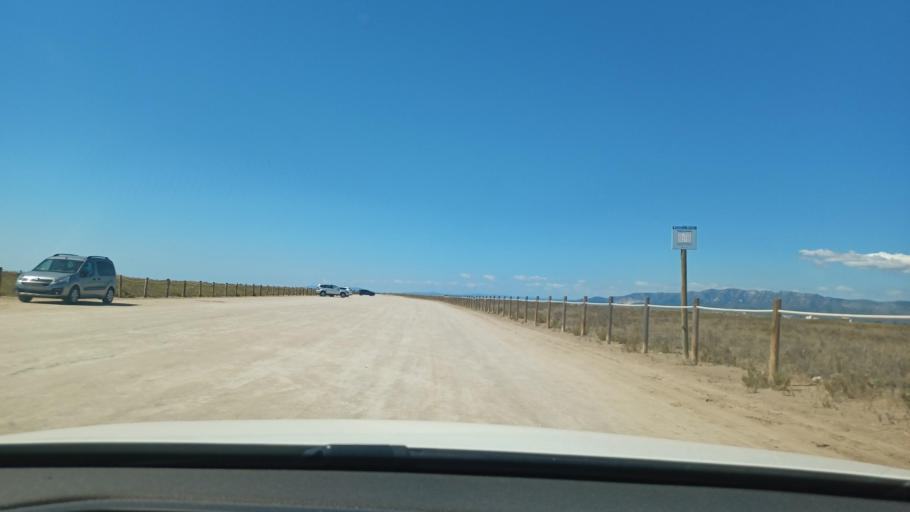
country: ES
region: Catalonia
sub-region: Provincia de Tarragona
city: Deltebre
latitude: 40.6456
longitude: 0.7620
